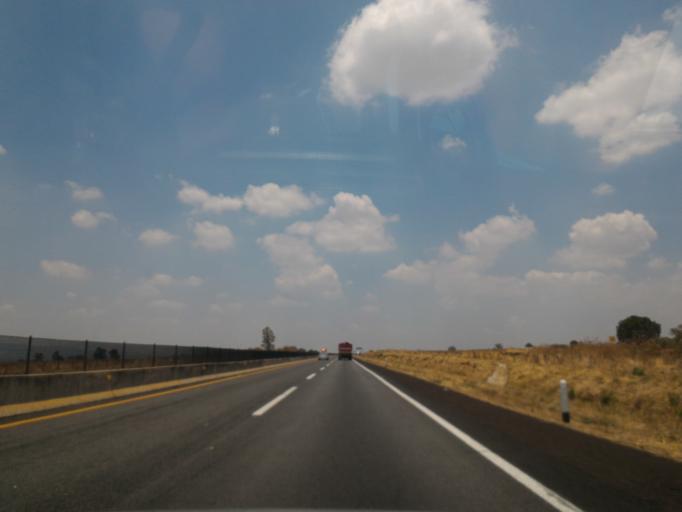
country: MX
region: Jalisco
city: Acatic
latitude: 20.7323
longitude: -102.9204
